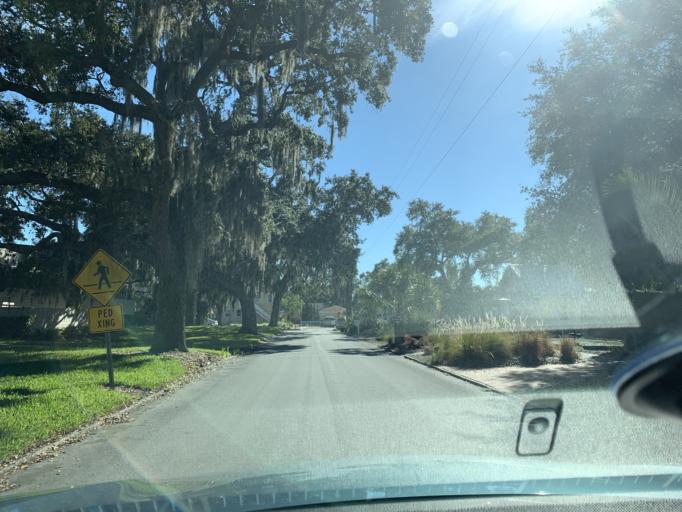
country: US
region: Florida
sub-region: Pinellas County
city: Gulfport
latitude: 27.7430
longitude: -82.7082
